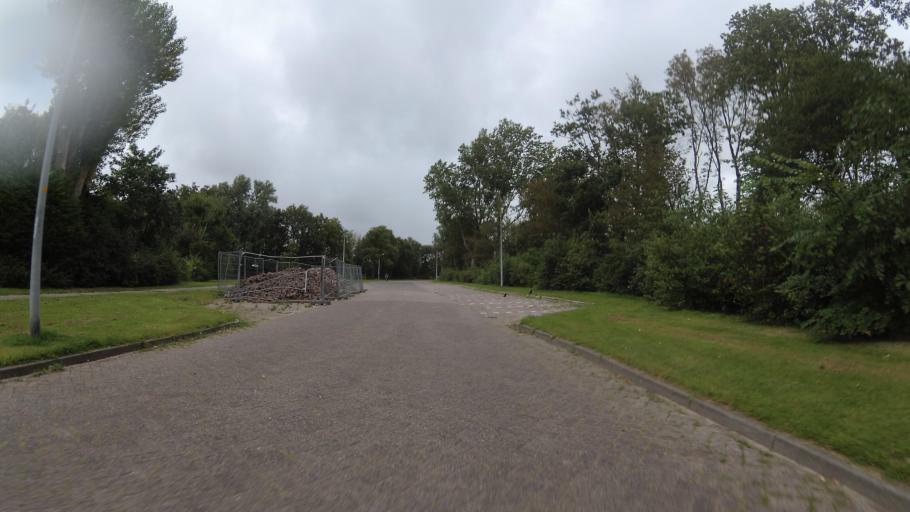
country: NL
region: North Holland
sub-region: Gemeente Den Helder
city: Den Helder
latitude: 52.9487
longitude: 4.7506
